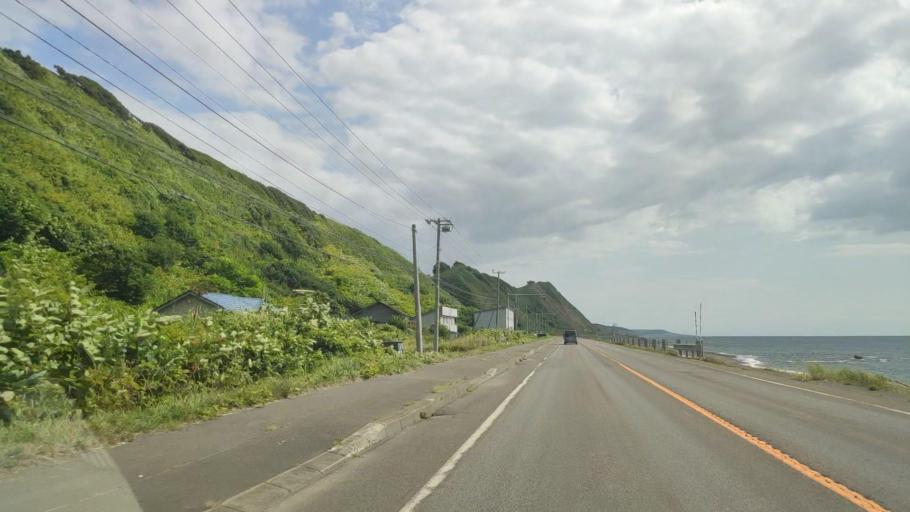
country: JP
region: Hokkaido
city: Rumoi
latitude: 44.2187
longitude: 141.6557
